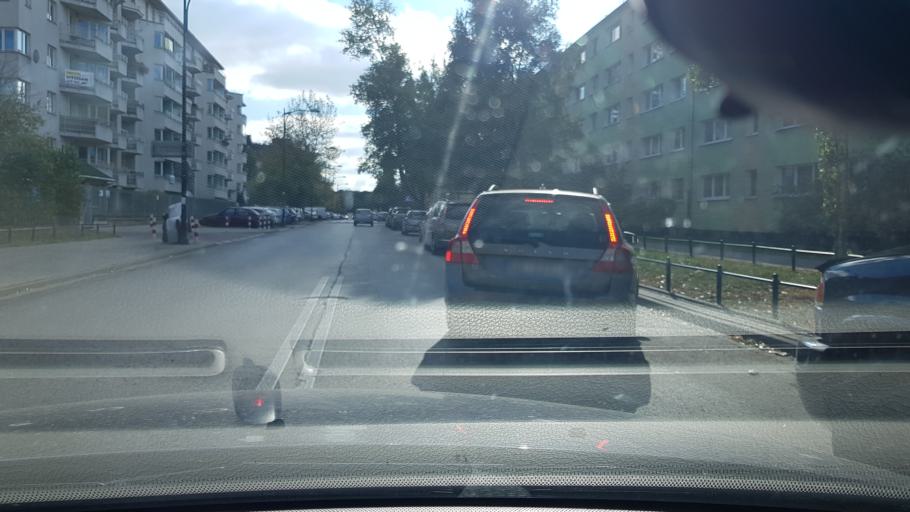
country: PL
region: Masovian Voivodeship
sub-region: Warszawa
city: Bielany
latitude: 52.2927
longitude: 20.9444
